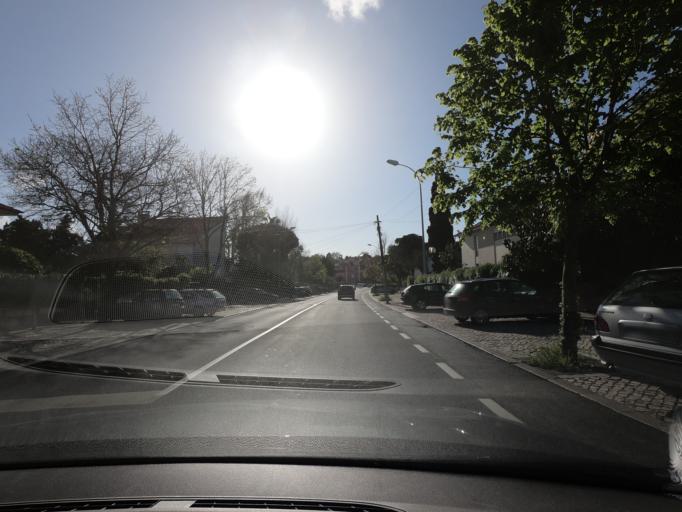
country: PT
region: Lisbon
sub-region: Oeiras
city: Carcavelos
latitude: 38.6909
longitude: -9.3170
